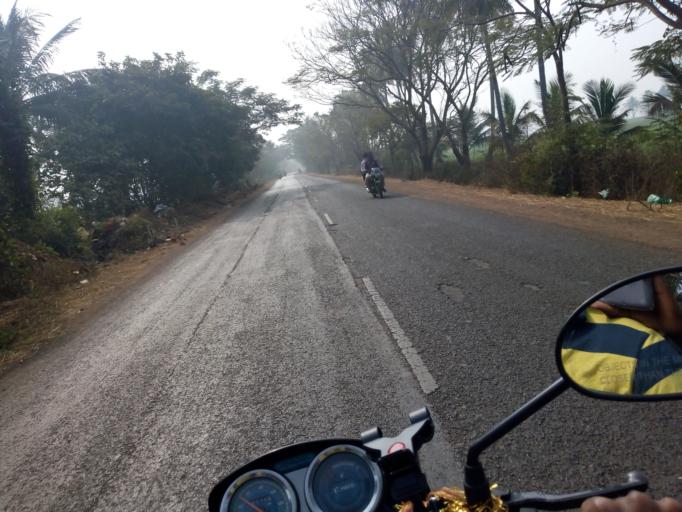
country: IN
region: Andhra Pradesh
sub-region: West Godavari
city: Tadepallegudem
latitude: 16.8067
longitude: 81.4096
